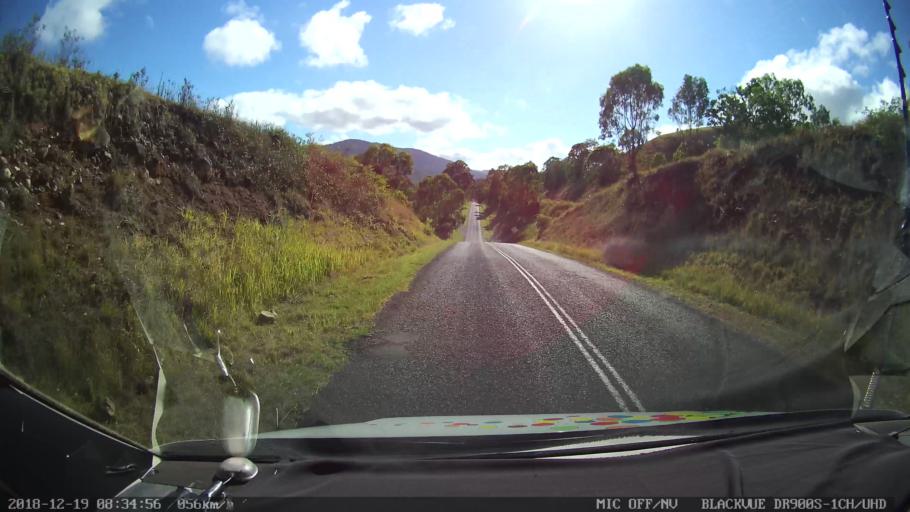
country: AU
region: New South Wales
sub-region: Kyogle
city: Kyogle
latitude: -28.3220
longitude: 152.9644
